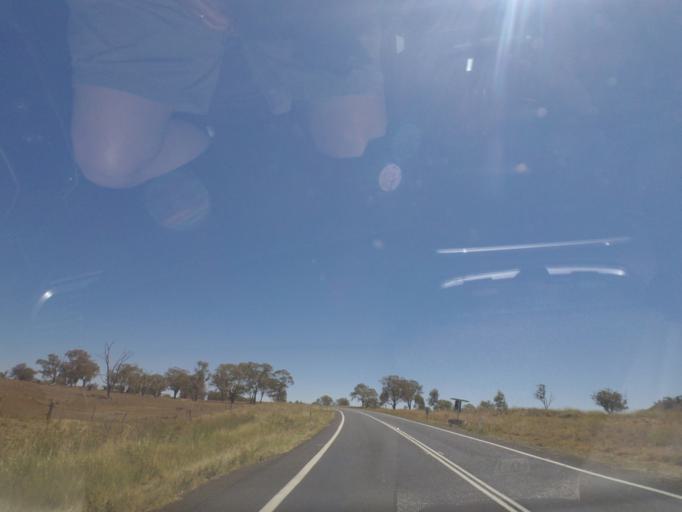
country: AU
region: New South Wales
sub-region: Warrumbungle Shire
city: Coonabarabran
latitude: -31.4378
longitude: 149.0431
